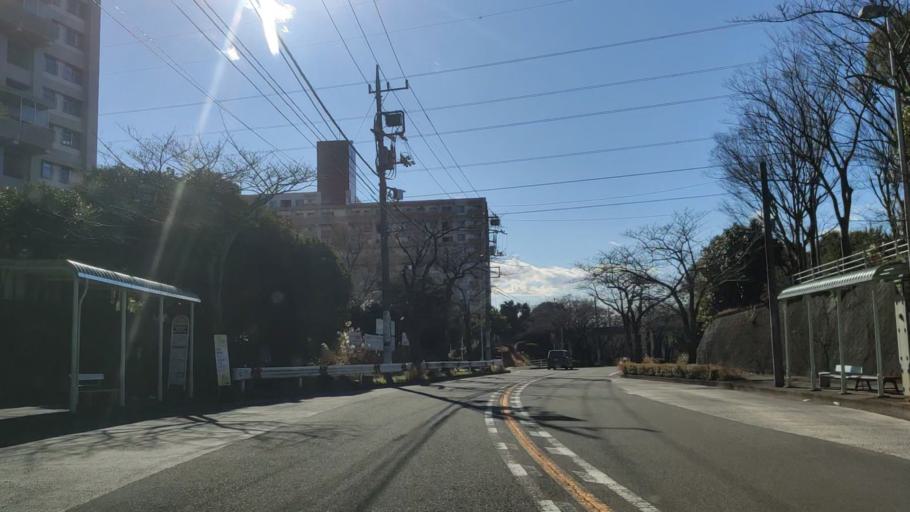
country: JP
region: Kanagawa
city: Minami-rinkan
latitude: 35.5031
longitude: 139.5043
